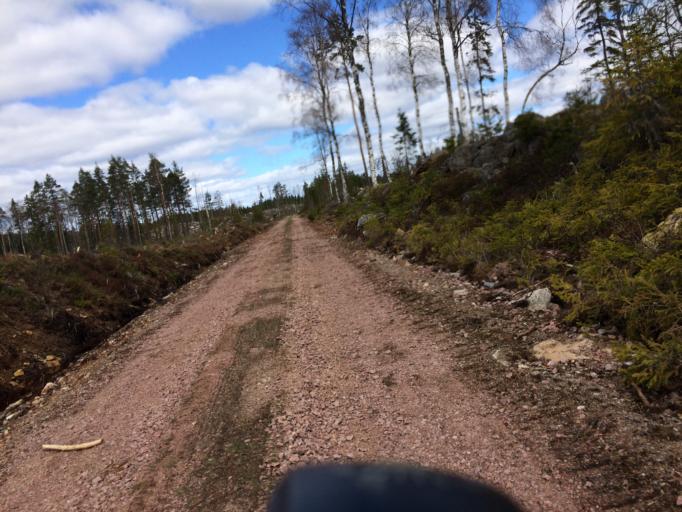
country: SE
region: OErebro
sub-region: Hallefors Kommun
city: Haellefors
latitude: 60.0500
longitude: 14.5251
